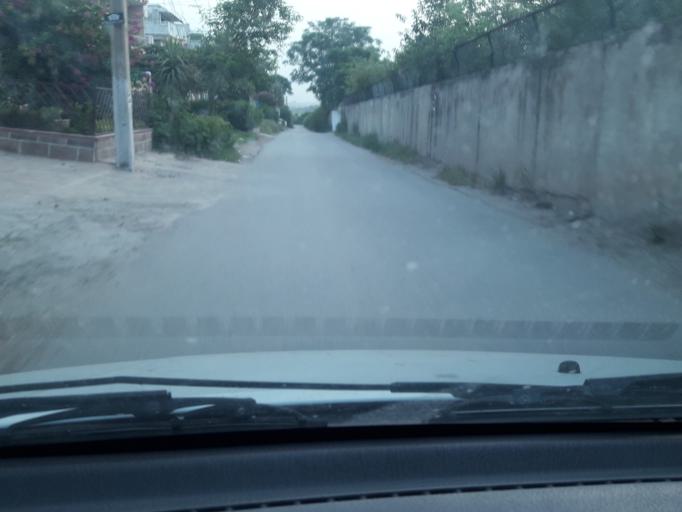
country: PK
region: Punjab
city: Rawalpindi
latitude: 33.6752
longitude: 73.1405
